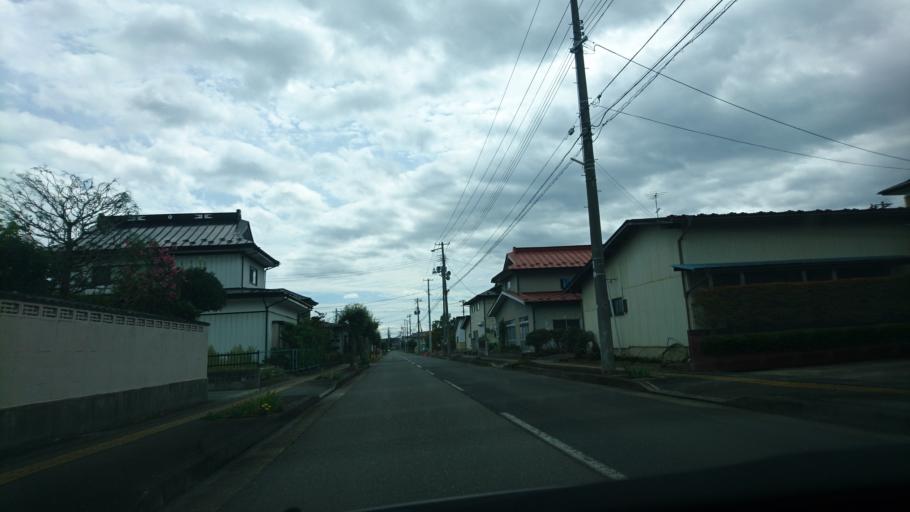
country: JP
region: Iwate
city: Ichinoseki
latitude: 38.9493
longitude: 141.1319
